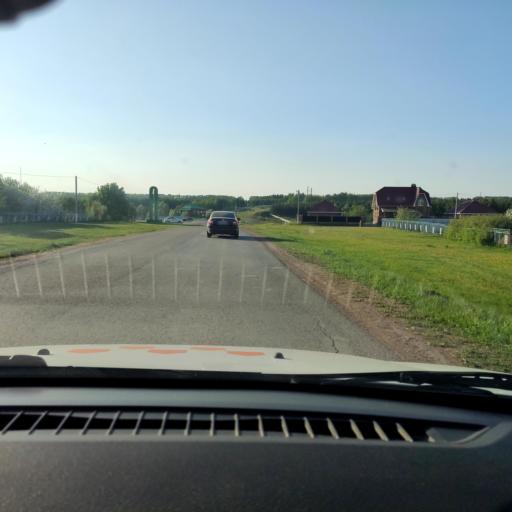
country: RU
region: Bashkortostan
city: Karmaskaly
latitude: 54.3690
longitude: 56.1556
